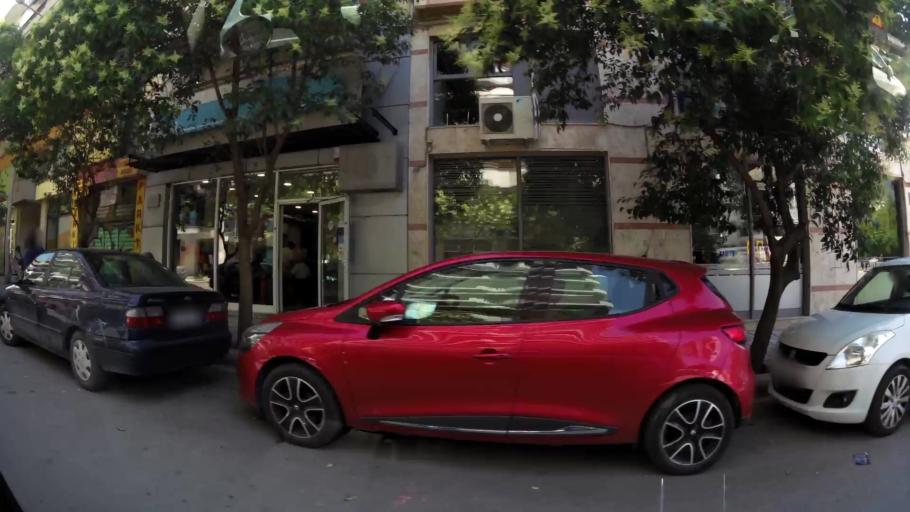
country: GR
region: Central Macedonia
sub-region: Nomos Thessalonikis
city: Triandria
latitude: 40.6049
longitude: 22.9599
